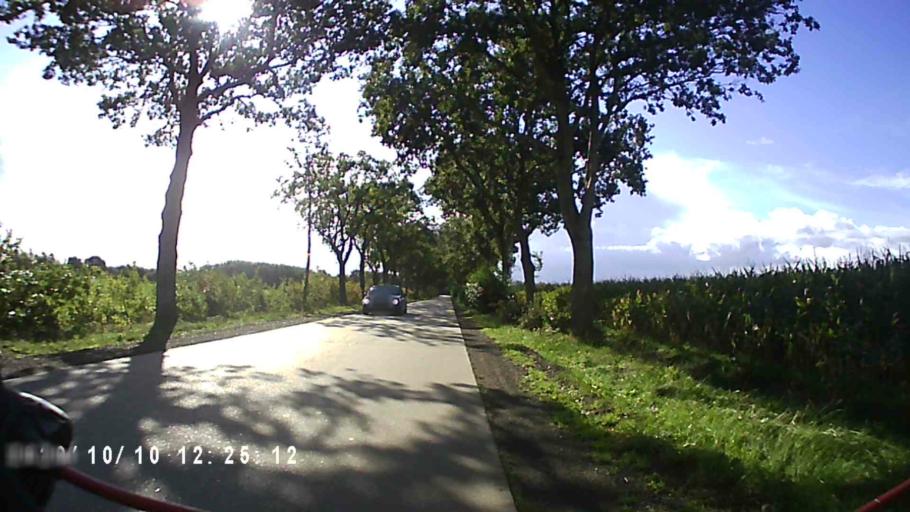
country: NL
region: Friesland
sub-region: Gemeente Heerenveen
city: Jubbega
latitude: 52.9900
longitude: 6.1800
